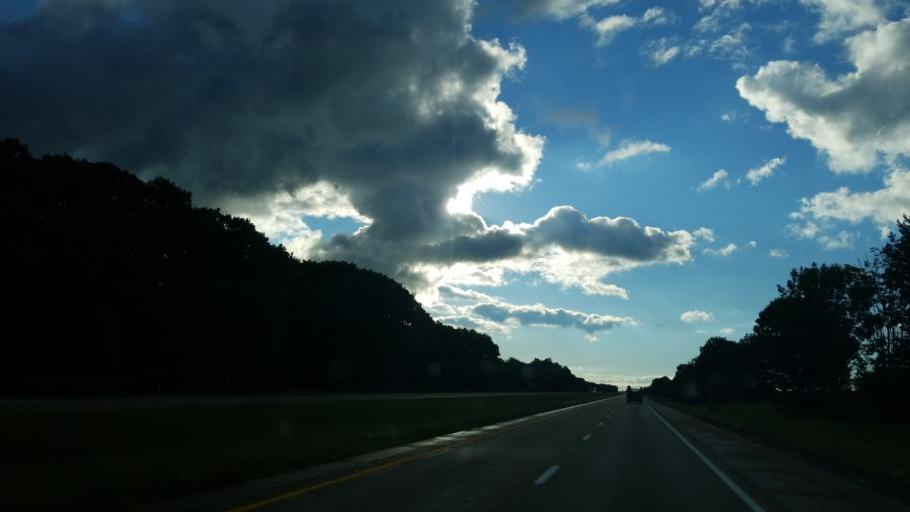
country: US
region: Ohio
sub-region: Ashtabula County
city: Geneva
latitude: 41.7699
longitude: -80.9277
